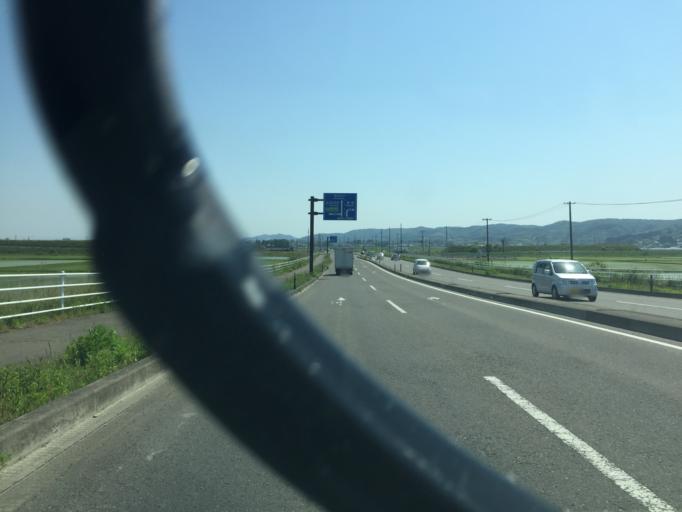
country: JP
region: Miyagi
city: Iwanuma
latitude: 38.1478
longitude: 140.8633
